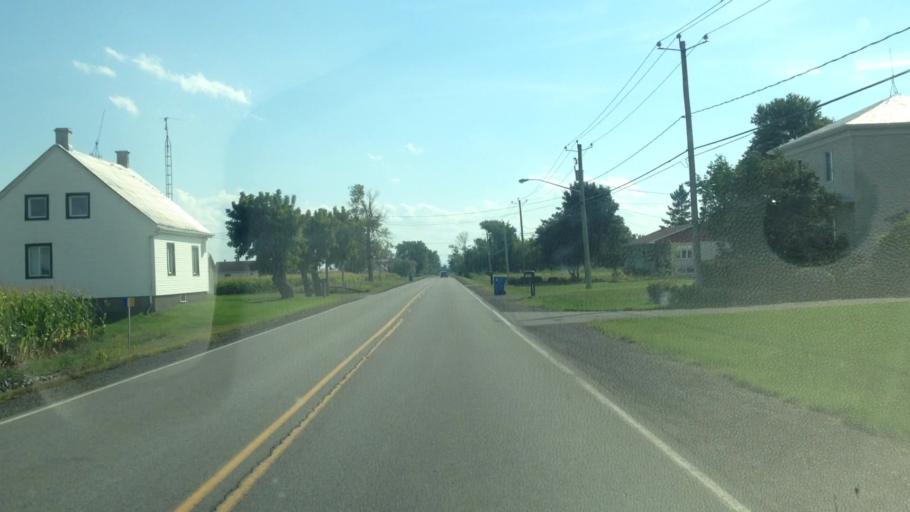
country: CA
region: Quebec
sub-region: Monteregie
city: Mercier
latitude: 45.2874
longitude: -73.6869
